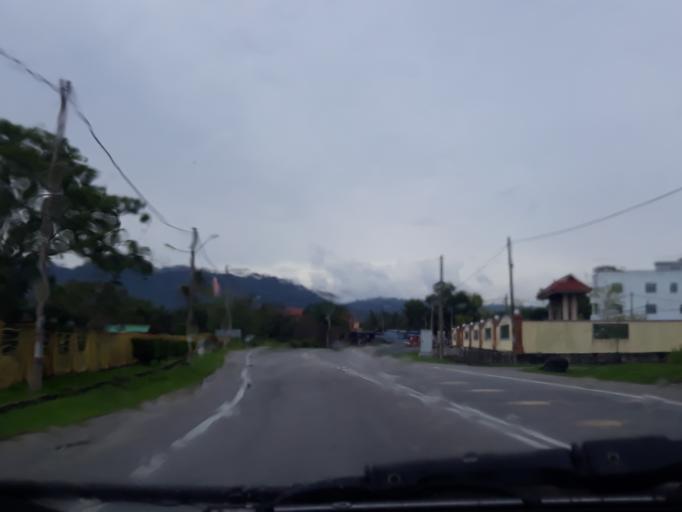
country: MY
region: Penang
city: Nibong Tebal
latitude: 5.2136
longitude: 100.6126
